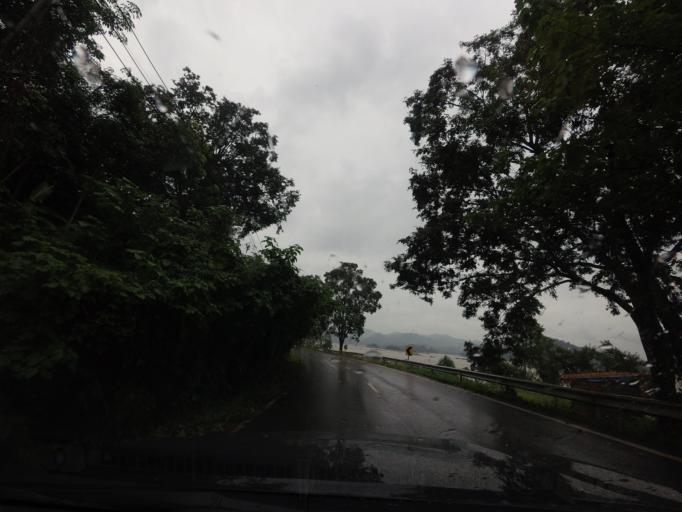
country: TH
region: Nong Khai
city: Sangkhom
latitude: 18.2029
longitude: 102.1594
